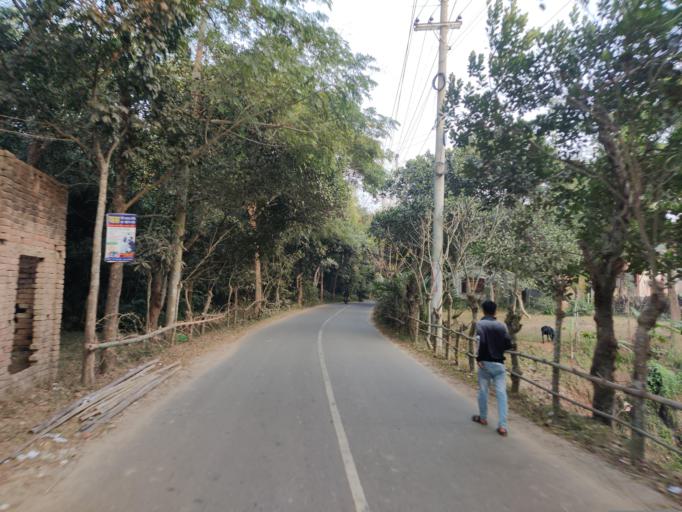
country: BD
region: Dhaka
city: Bajitpur
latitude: 24.1573
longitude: 90.7674
